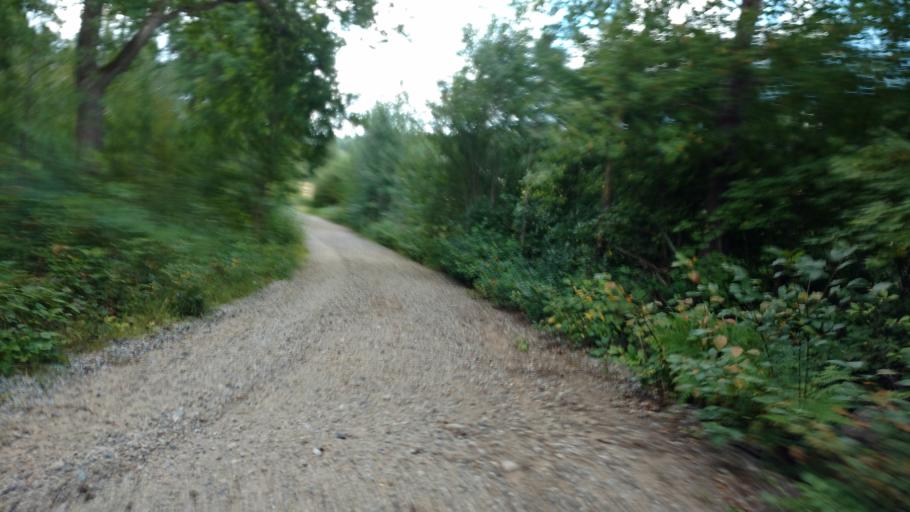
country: FI
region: Varsinais-Suomi
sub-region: Salo
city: Salo
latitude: 60.3523
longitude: 23.1574
